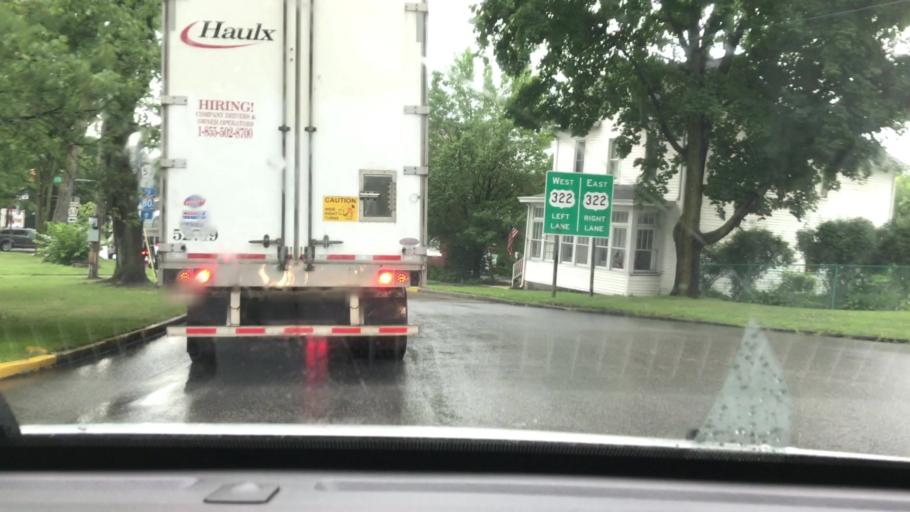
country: US
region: Pennsylvania
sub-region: Centre County
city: Philipsburg
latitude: 40.8960
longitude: -78.2200
